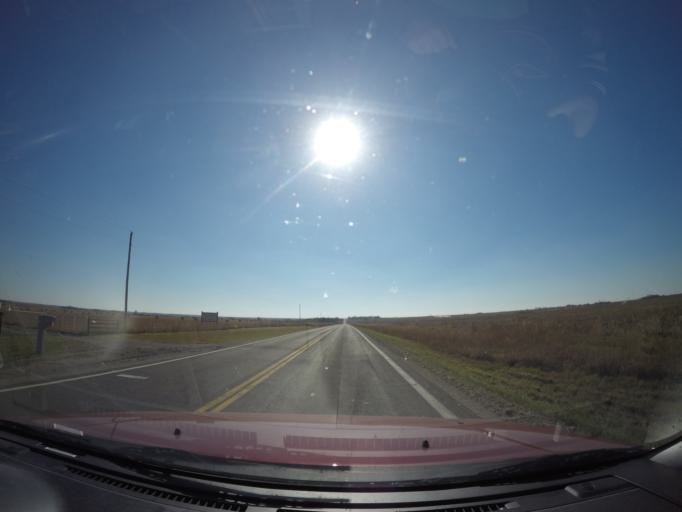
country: US
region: Kansas
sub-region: Morris County
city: Council Grove
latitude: 38.7821
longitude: -96.5013
